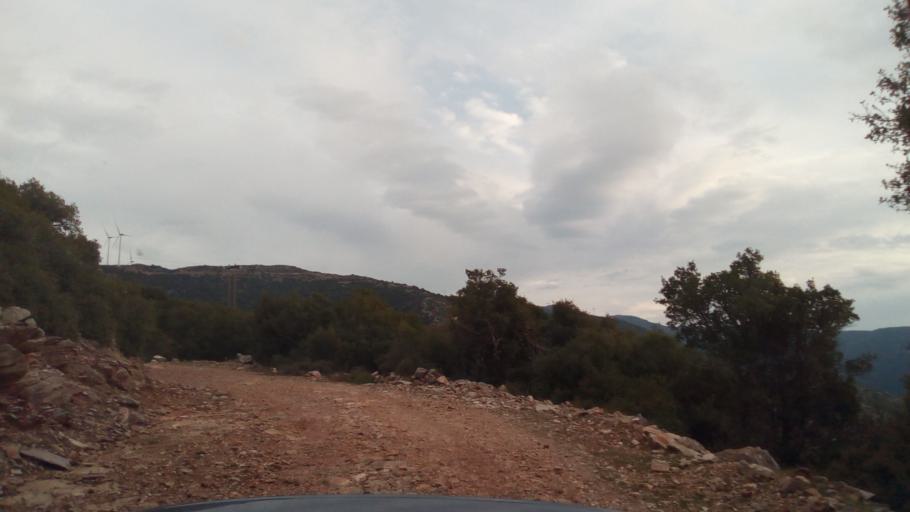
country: GR
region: West Greece
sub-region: Nomos Achaias
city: Kamarai
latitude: 38.4111
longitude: 22.0428
